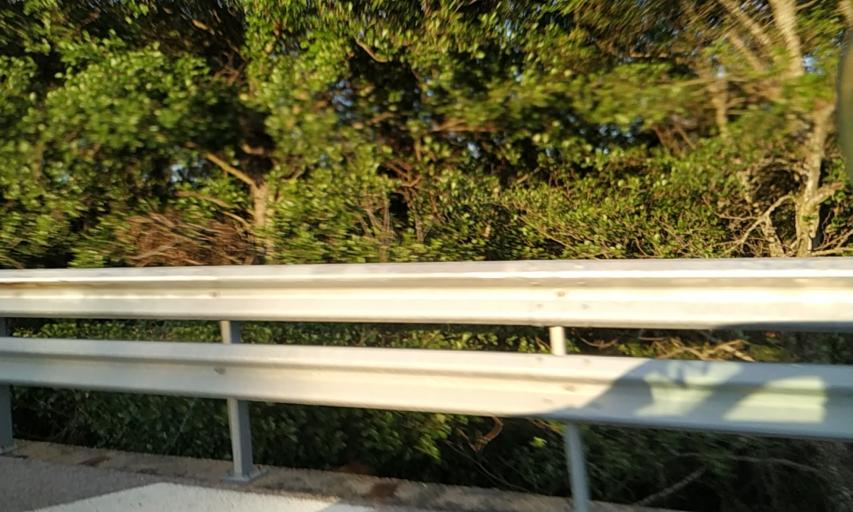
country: ES
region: Extremadura
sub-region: Provincia de Caceres
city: Valencia de Alcantara
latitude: 39.3865
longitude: -7.2476
